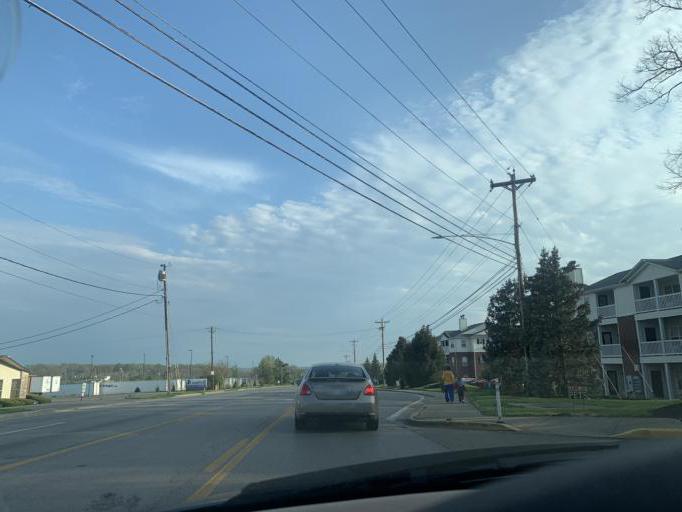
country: US
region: Ohio
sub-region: Hamilton County
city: Woodlawn
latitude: 39.2635
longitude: -84.4693
